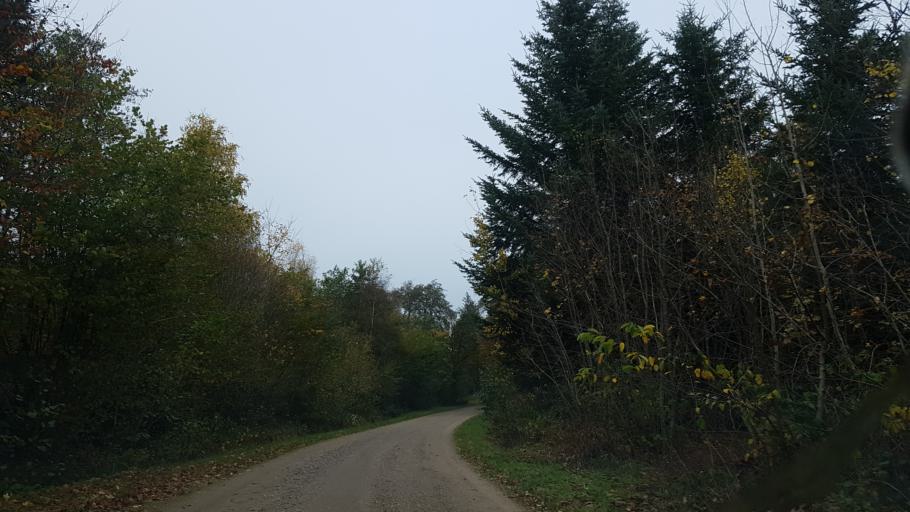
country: DK
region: South Denmark
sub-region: Tonder Kommune
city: Sherrebek
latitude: 55.1904
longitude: 8.7567
